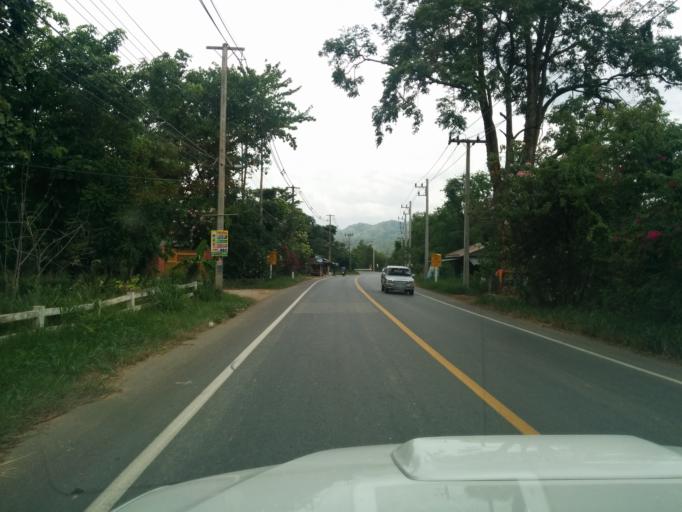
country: TH
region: Sara Buri
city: Muak Lek
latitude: 14.5988
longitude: 101.2152
